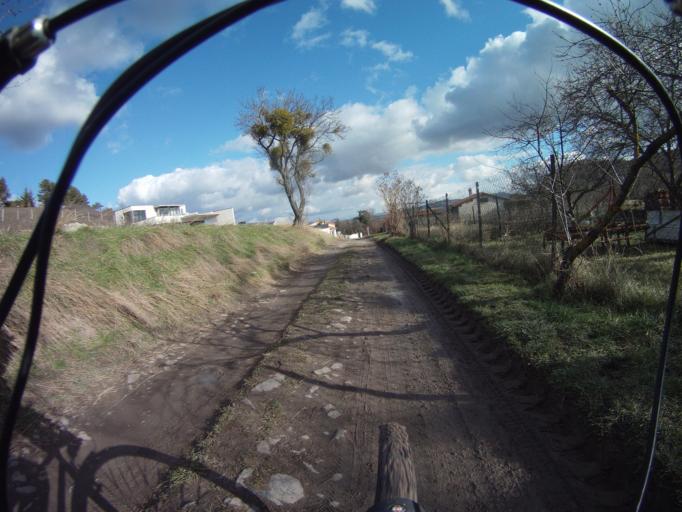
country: FR
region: Auvergne
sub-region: Departement du Puy-de-Dome
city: Perignat-les-Sarlieve
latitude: 45.7367
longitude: 3.1324
